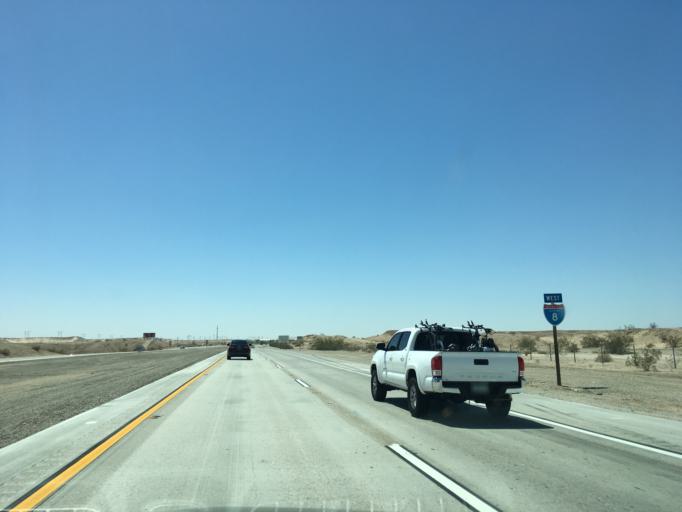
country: MX
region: Baja California
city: Los Algodones
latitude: 32.7443
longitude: -114.7262
